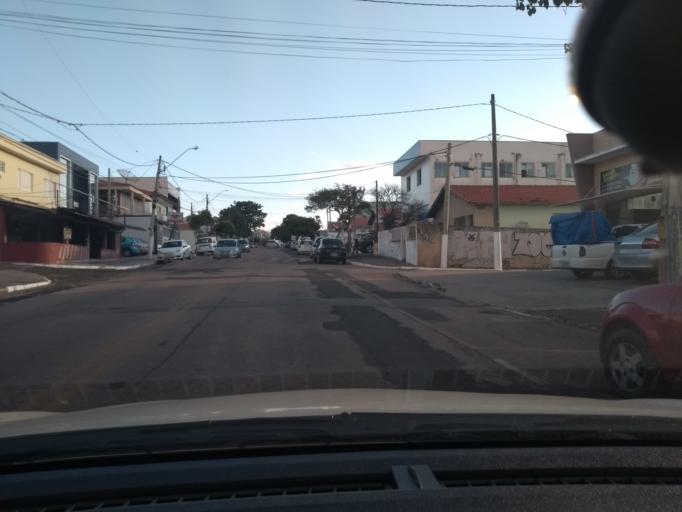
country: BR
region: Sao Paulo
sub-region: Itupeva
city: Itupeva
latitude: -23.1566
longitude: -47.0594
